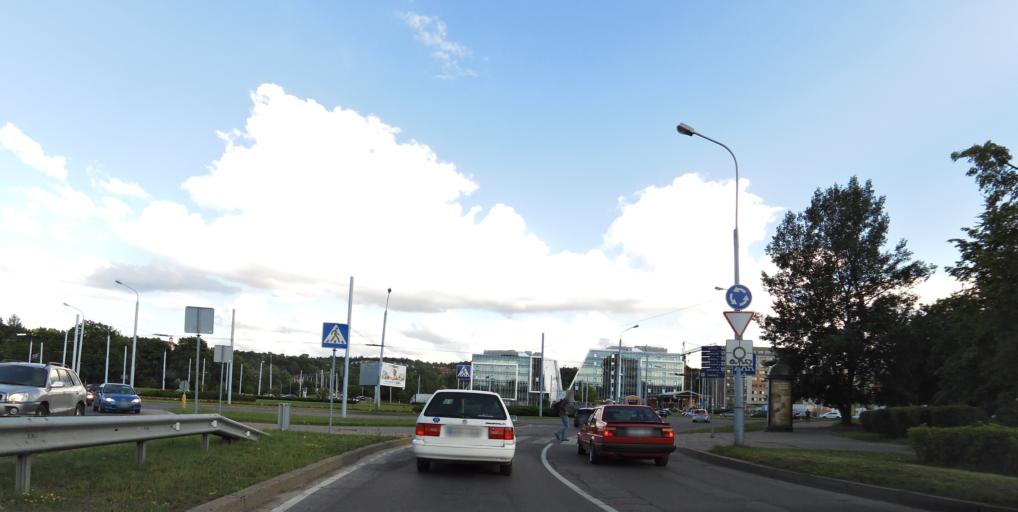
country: LT
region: Vilnius County
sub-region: Vilnius
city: Vilnius
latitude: 54.6968
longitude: 25.2975
